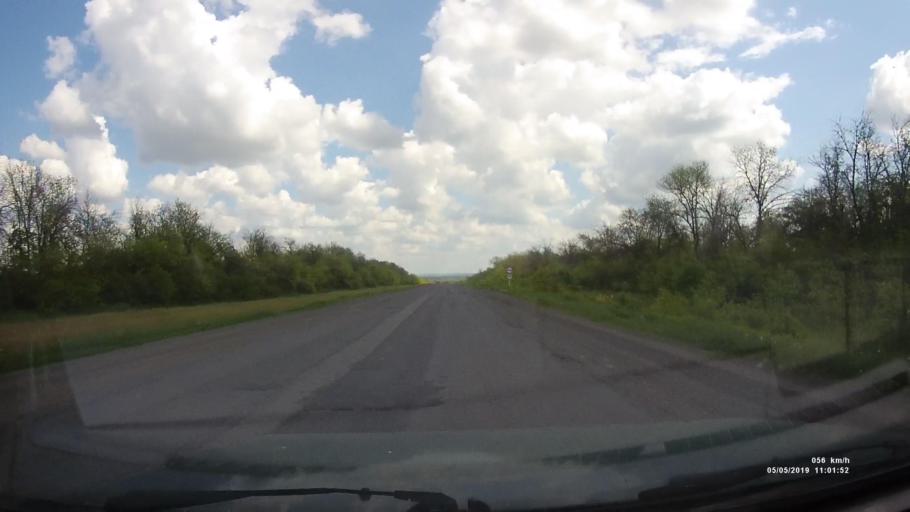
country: RU
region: Rostov
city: Ust'-Donetskiy
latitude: 47.6816
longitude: 40.9028
